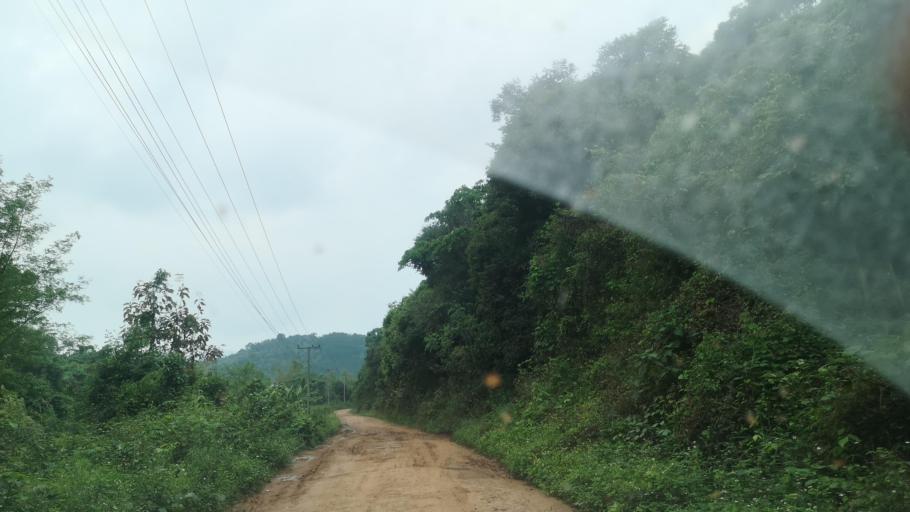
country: LA
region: Oudomxai
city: Muang La
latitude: 21.0753
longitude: 101.8367
